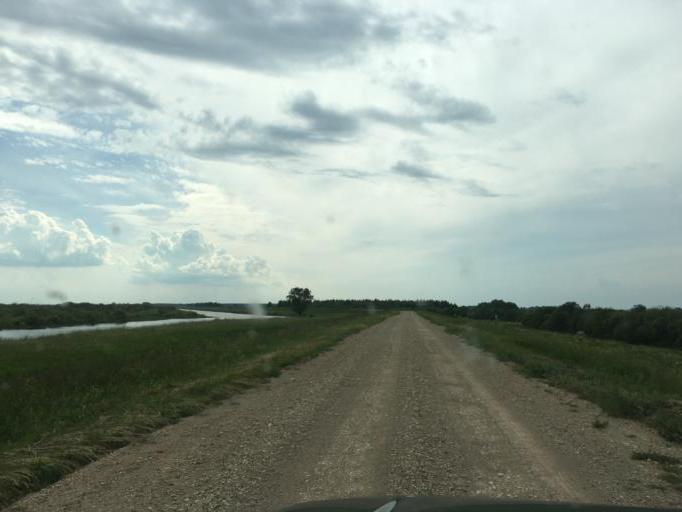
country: LV
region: Lubana
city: Lubana
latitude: 56.8033
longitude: 26.8397
